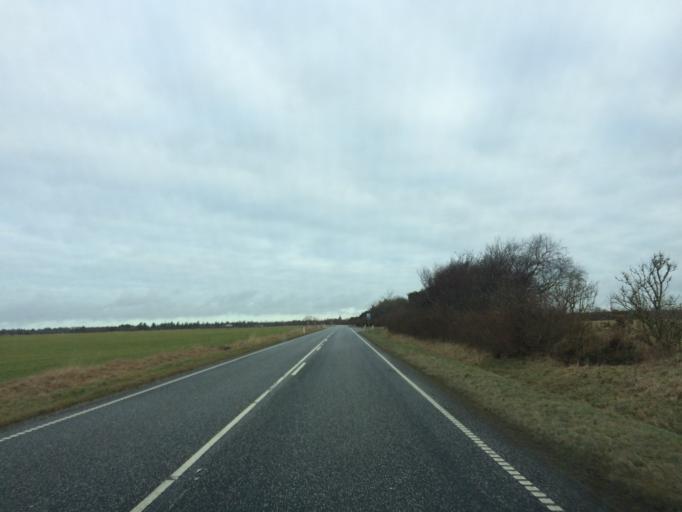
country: DK
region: Central Jutland
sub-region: Holstebro Kommune
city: Ulfborg
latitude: 56.3744
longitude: 8.4434
